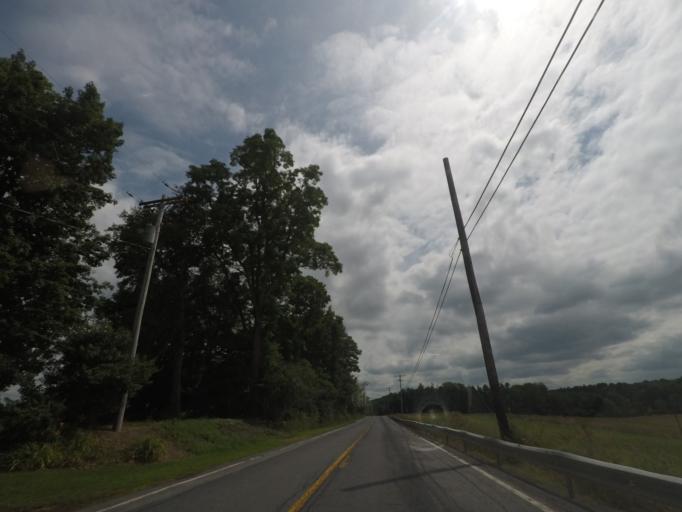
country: US
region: New York
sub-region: Saratoga County
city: Stillwater
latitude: 43.0204
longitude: -73.6452
